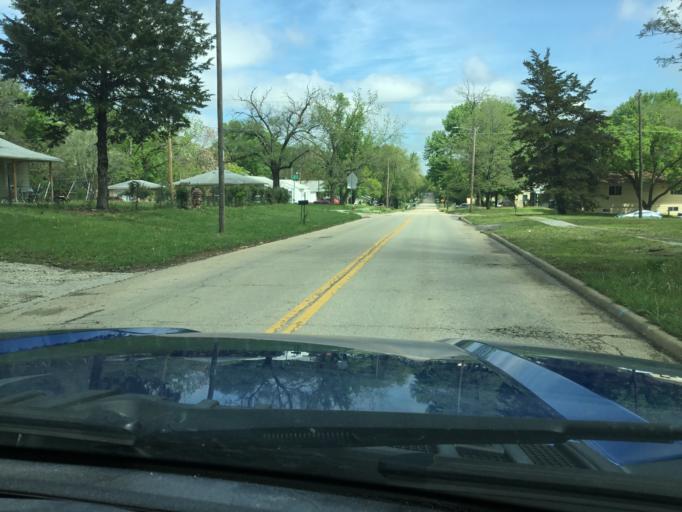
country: US
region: Kansas
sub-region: Shawnee County
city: Topeka
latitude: 39.0202
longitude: -95.6608
